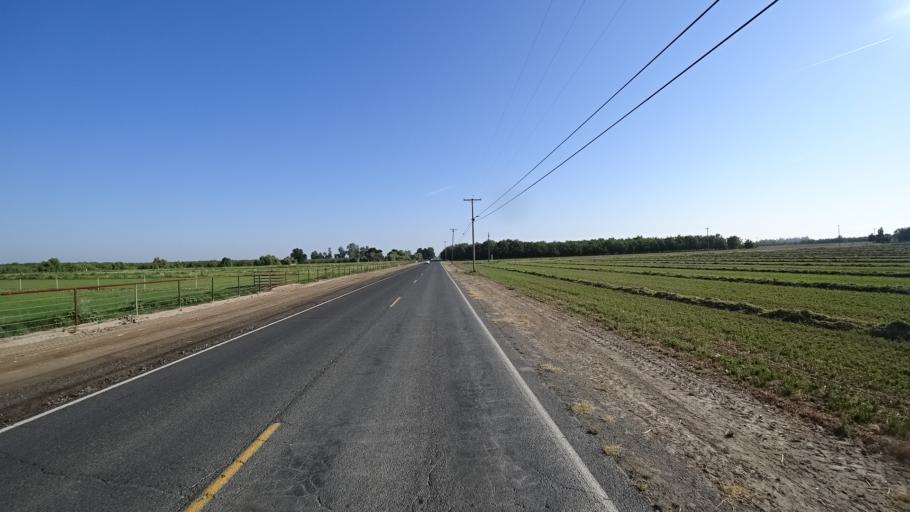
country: US
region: California
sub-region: Kings County
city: Armona
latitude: 36.2783
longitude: -119.7091
